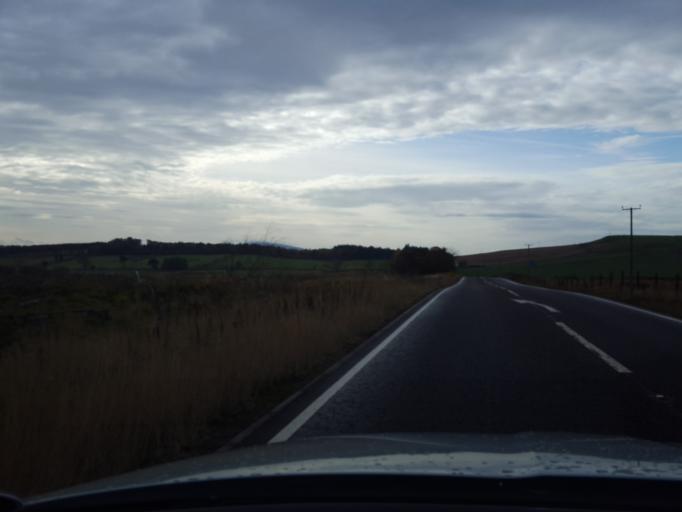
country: GB
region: Scotland
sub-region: South Lanarkshire
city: Carnwath
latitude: 55.7262
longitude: -3.5766
